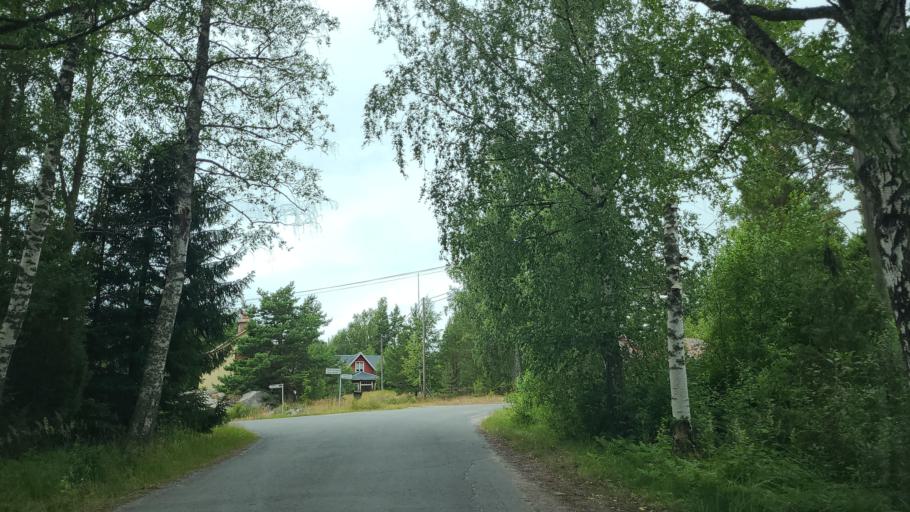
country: FI
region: Varsinais-Suomi
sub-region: Aboland-Turunmaa
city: Dragsfjaerd
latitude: 60.0976
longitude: 22.4322
